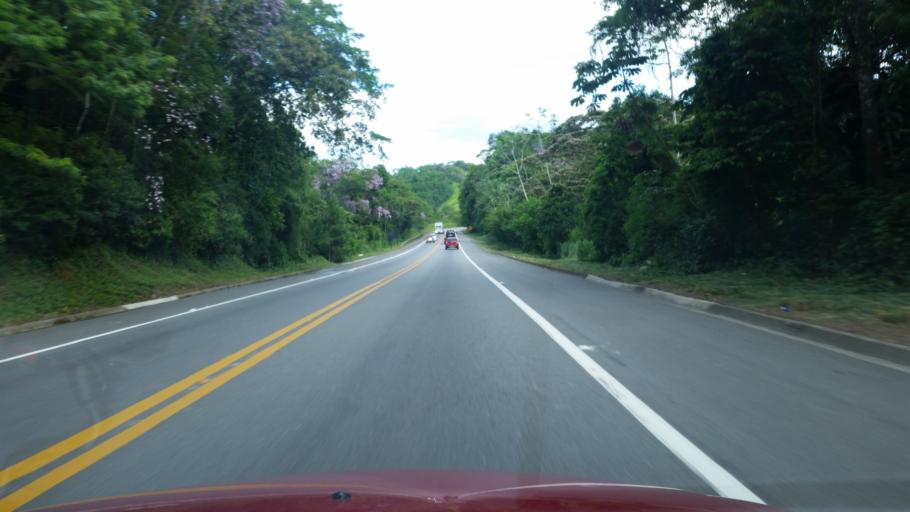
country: BR
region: Sao Paulo
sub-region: Miracatu
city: Miracatu
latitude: -24.2669
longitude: -47.2701
